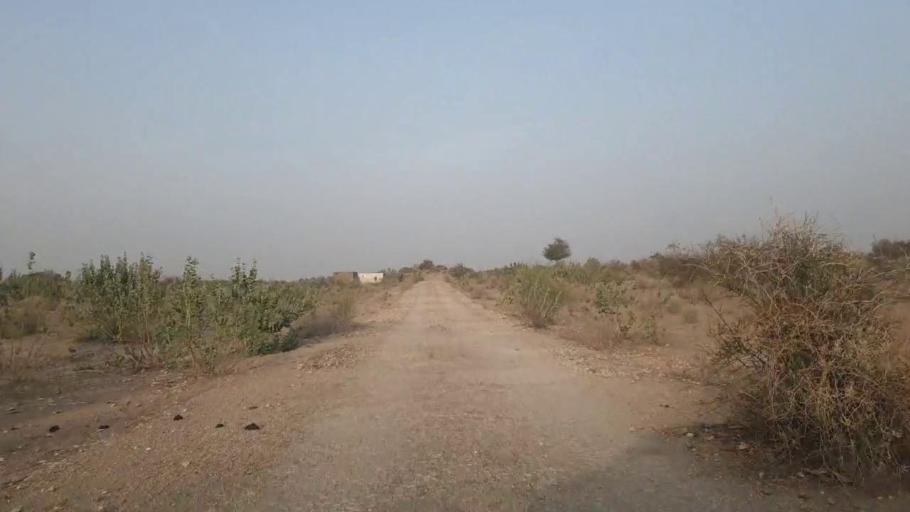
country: PK
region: Sindh
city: Chor
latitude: 25.5251
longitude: 69.9599
